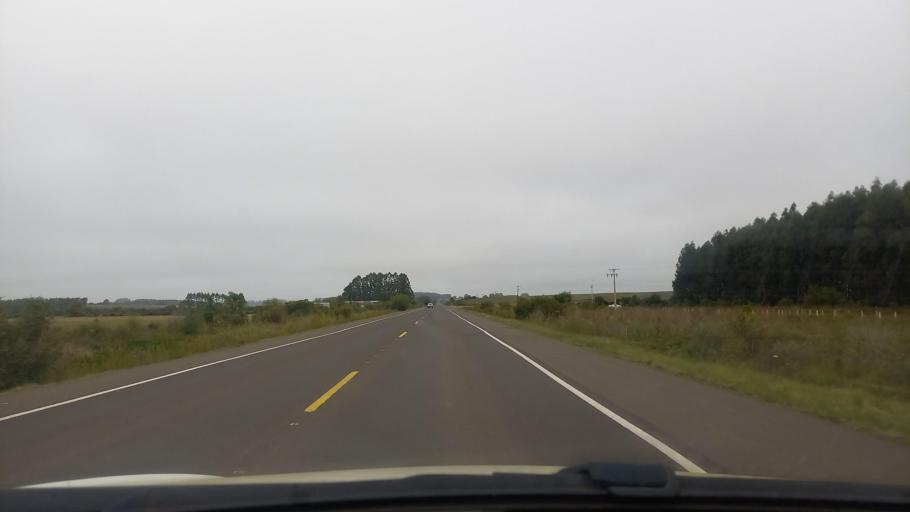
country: BR
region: Rio Grande do Sul
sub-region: Rosario Do Sul
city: Rosario do Sul
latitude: -30.2990
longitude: -54.9902
